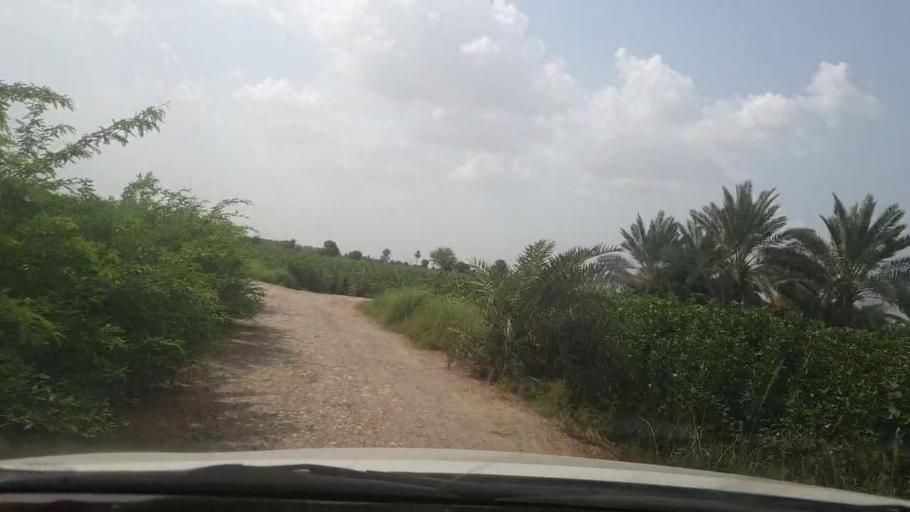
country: PK
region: Sindh
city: Kot Diji
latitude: 27.3352
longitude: 69.0073
